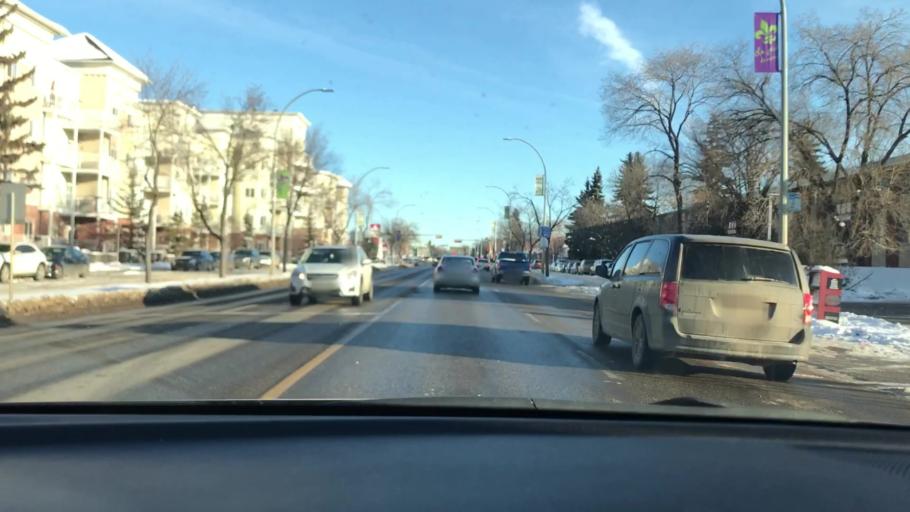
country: CA
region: Alberta
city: Edmonton
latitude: 53.5180
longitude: -113.4612
